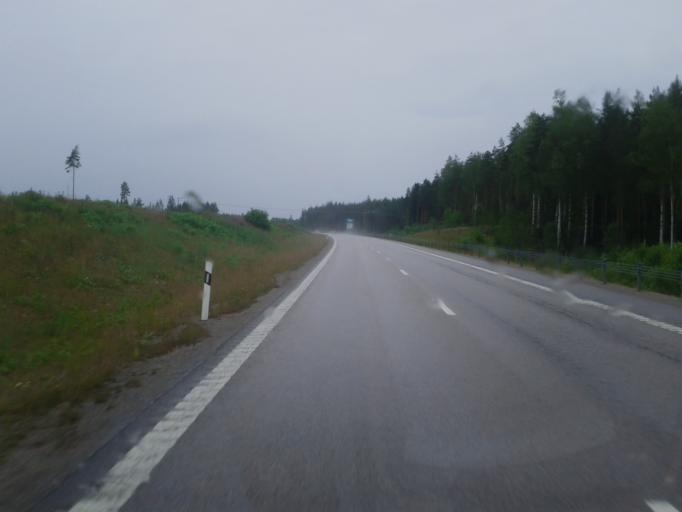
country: SE
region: Uppsala
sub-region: Tierps Kommun
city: Tierp
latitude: 60.3087
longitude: 17.5221
